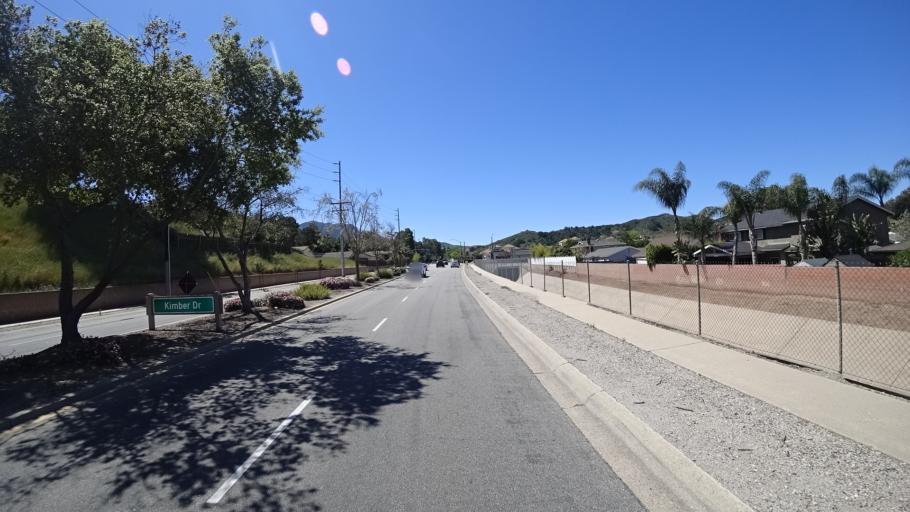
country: US
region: California
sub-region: Ventura County
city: Casa Conejo
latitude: 34.1729
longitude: -118.9545
